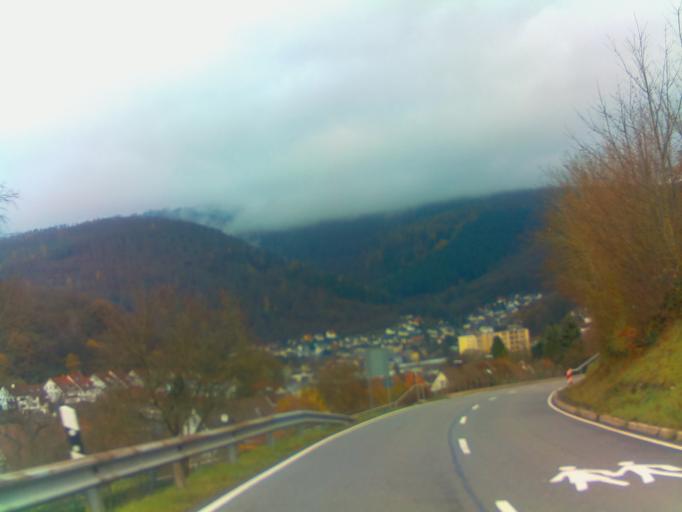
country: DE
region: Baden-Wuerttemberg
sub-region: Karlsruhe Region
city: Eberbach
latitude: 49.4663
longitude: 8.9953
